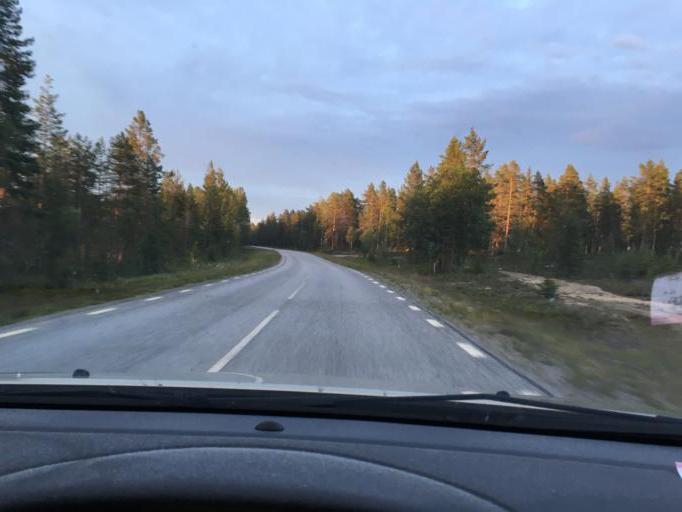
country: SE
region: Norrbotten
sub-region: Kalix Kommun
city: Toere
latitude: 66.0522
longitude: 22.4888
